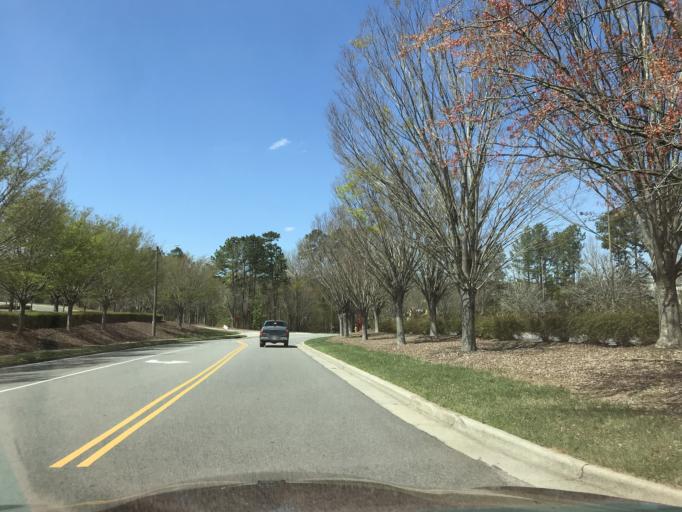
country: US
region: North Carolina
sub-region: Wake County
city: West Raleigh
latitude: 35.8713
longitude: -78.7175
